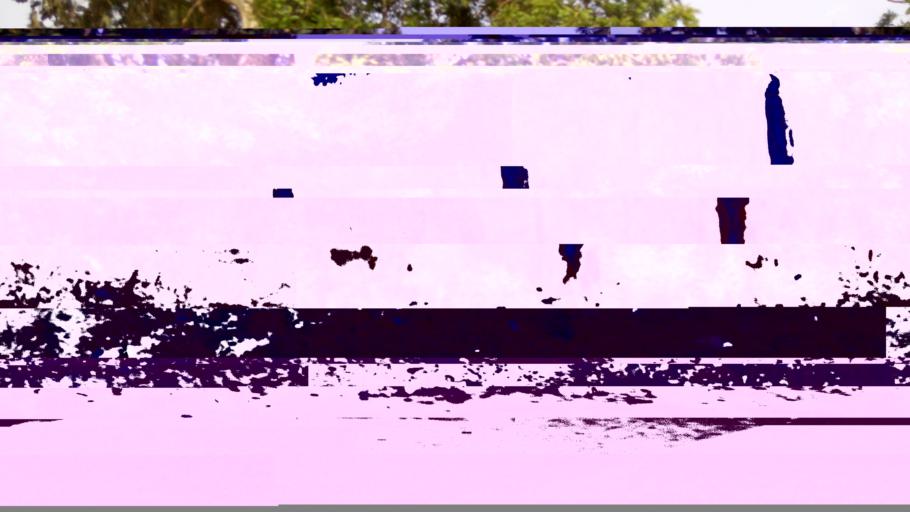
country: TG
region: Maritime
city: Tsevie
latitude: 6.3797
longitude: 1.2041
